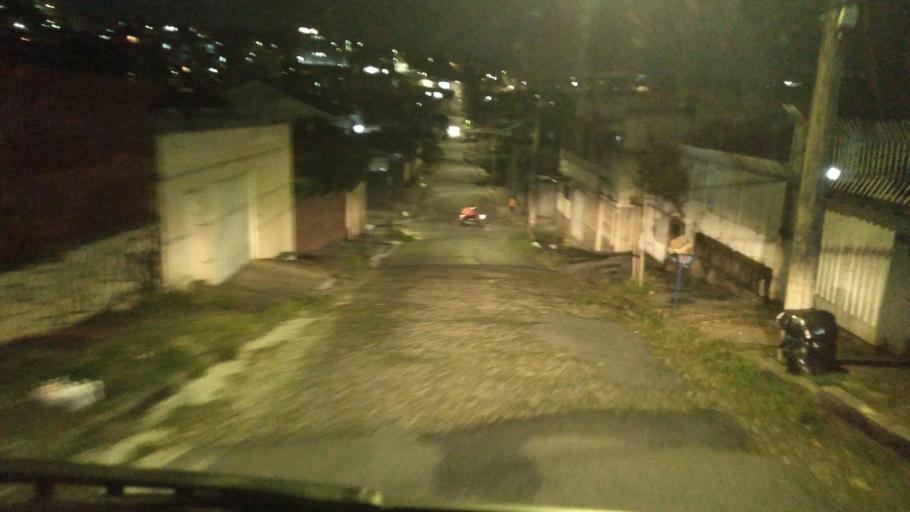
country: BR
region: Minas Gerais
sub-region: Belo Horizonte
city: Belo Horizonte
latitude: -19.8921
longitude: -43.9388
